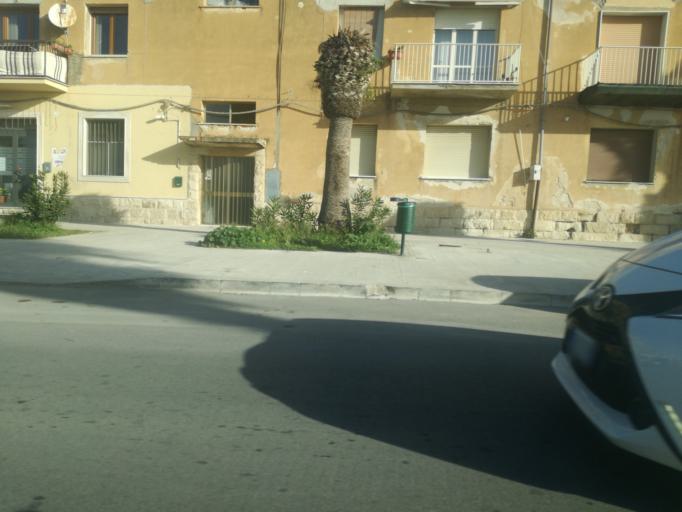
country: IT
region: Sicily
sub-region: Provincia di Caltanissetta
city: Gela
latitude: 37.0648
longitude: 14.2466
